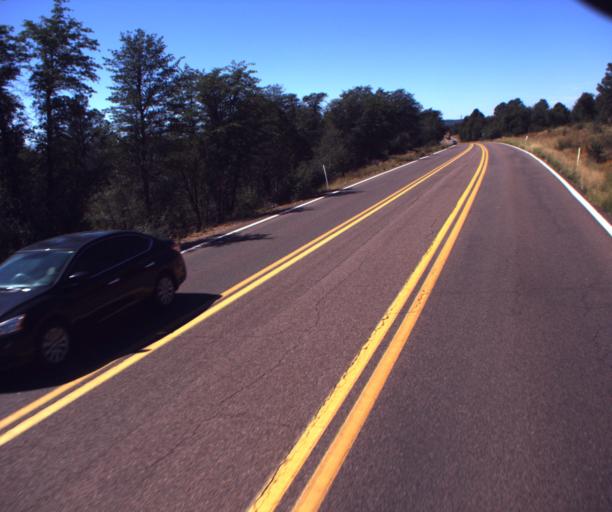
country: US
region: Arizona
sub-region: Gila County
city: Star Valley
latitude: 34.2647
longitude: -111.2337
